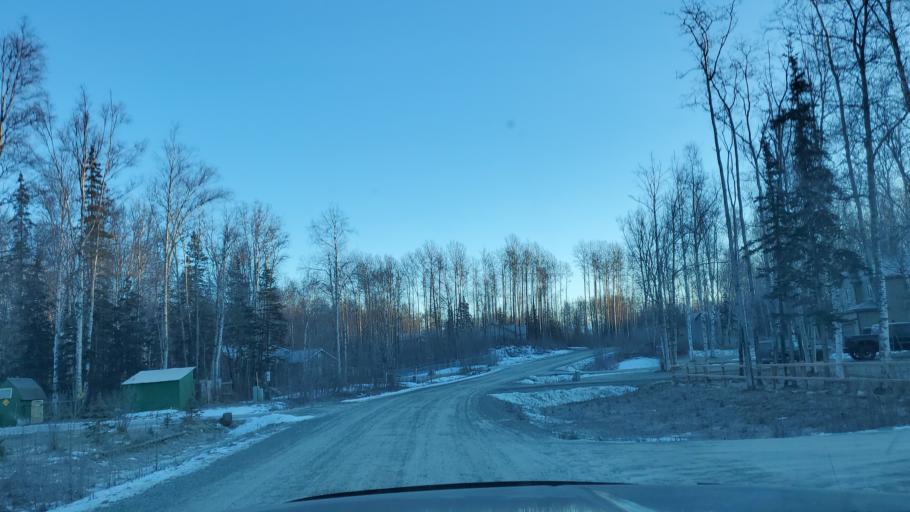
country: US
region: Alaska
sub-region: Matanuska-Susitna Borough
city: Lakes
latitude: 61.6559
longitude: -149.3392
